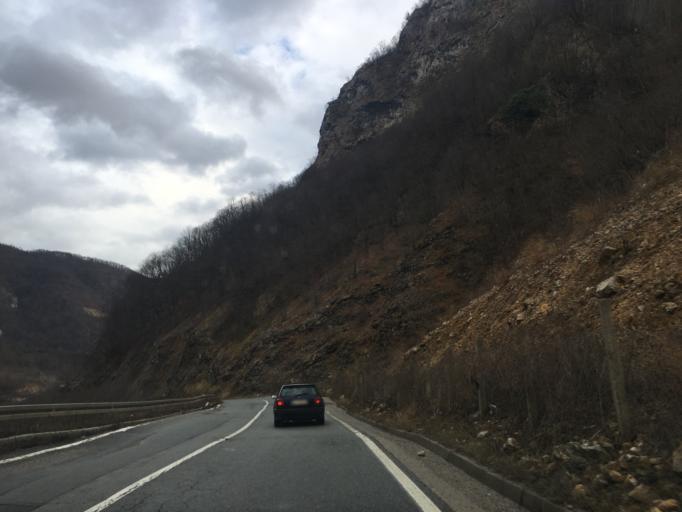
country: RS
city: Sokolovo Brdo
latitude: 43.1603
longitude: 19.7730
